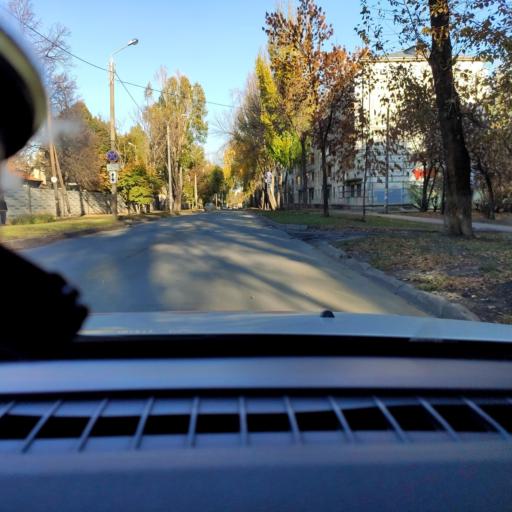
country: RU
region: Samara
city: Samara
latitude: 53.2100
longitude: 50.2331
